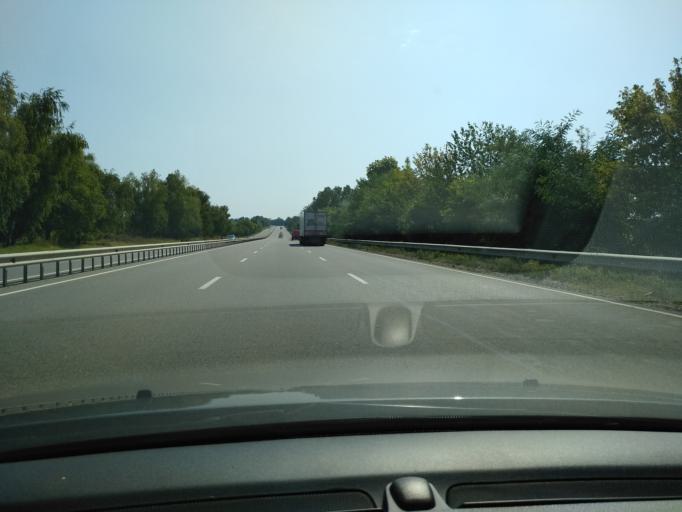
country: MD
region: Chisinau
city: Cricova
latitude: 47.1243
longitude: 28.8501
